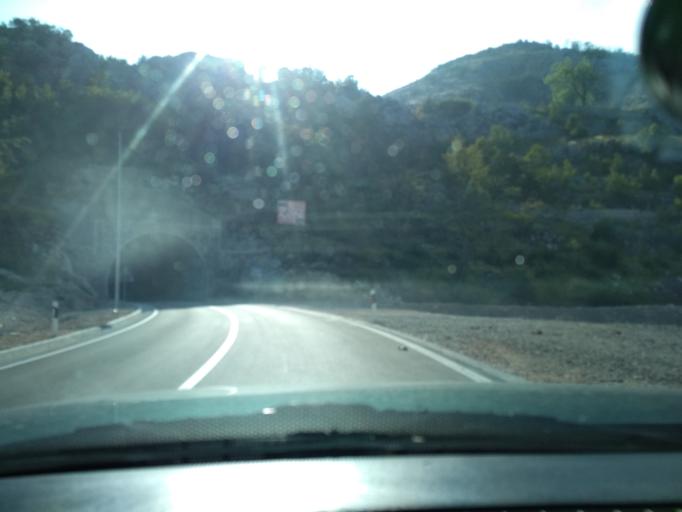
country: ME
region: Cetinje
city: Cetinje
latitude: 42.4378
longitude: 18.8533
